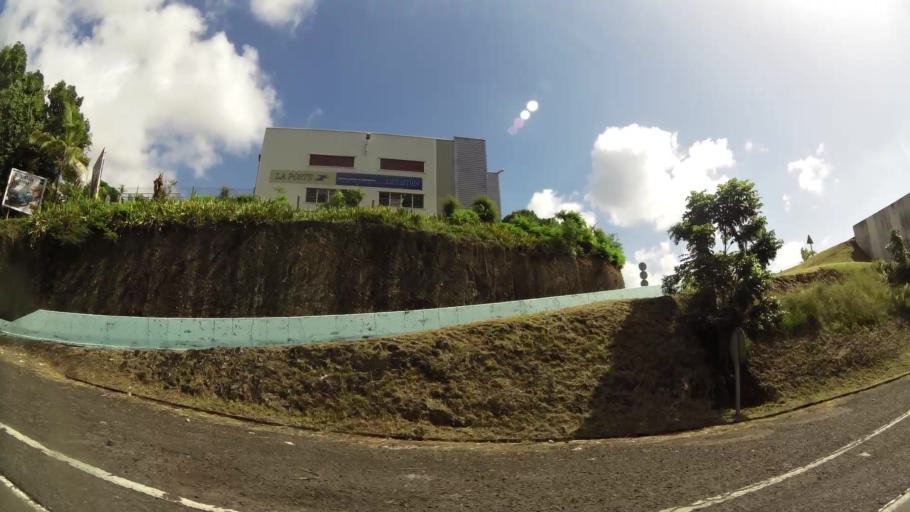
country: MQ
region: Martinique
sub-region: Martinique
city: Fort-de-France
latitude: 14.6056
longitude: -61.0880
